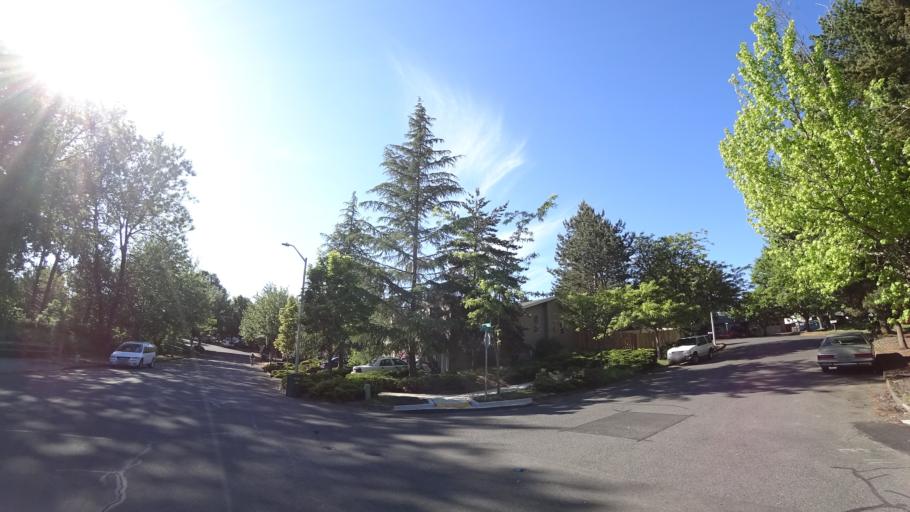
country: US
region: Oregon
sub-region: Washington County
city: Beaverton
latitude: 45.4562
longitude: -122.8125
